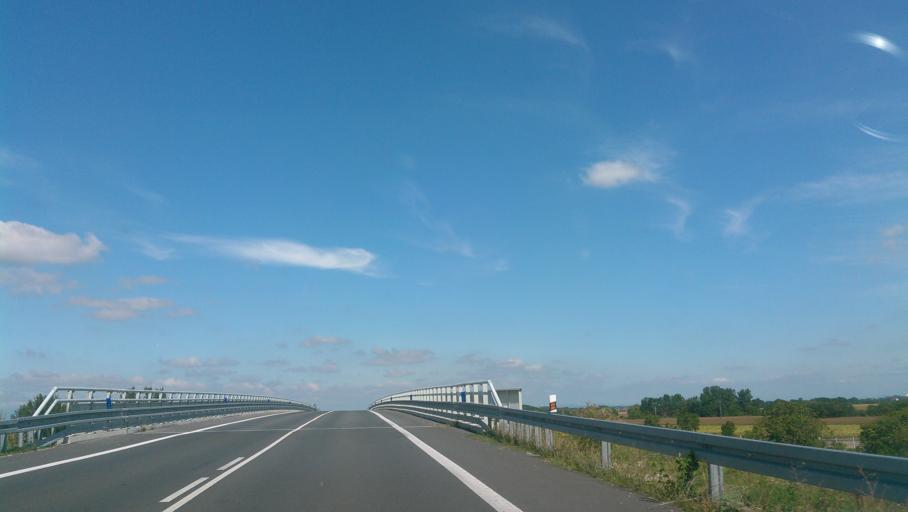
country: SK
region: Trnavsky
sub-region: Okres Galanta
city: Galanta
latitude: 48.1856
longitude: 17.7007
